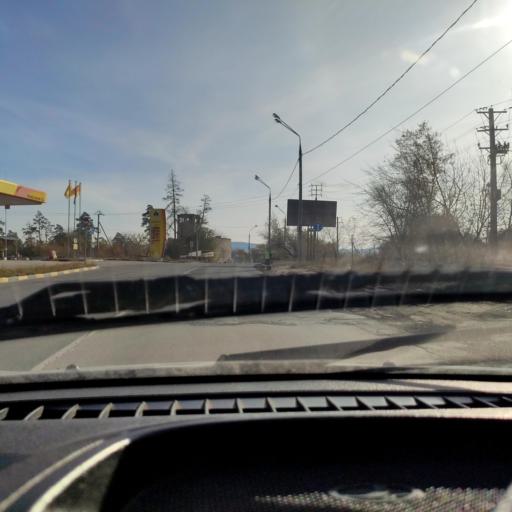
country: RU
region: Samara
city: Zhigulevsk
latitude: 53.4680
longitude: 49.5480
